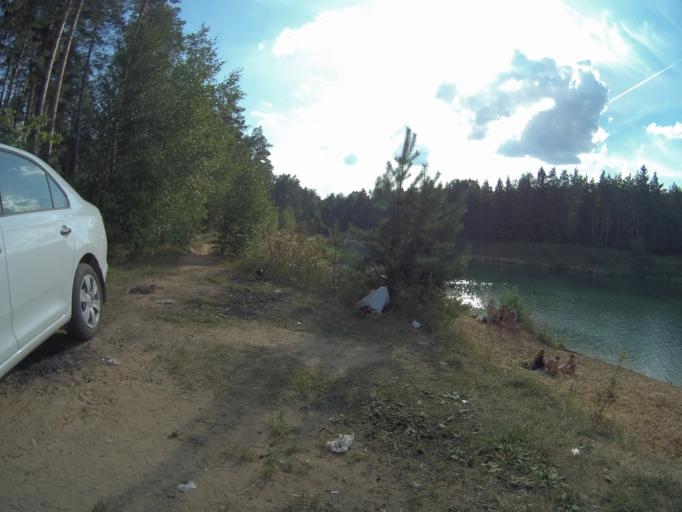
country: RU
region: Vladimir
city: Golovino
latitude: 56.0324
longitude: 40.4100
